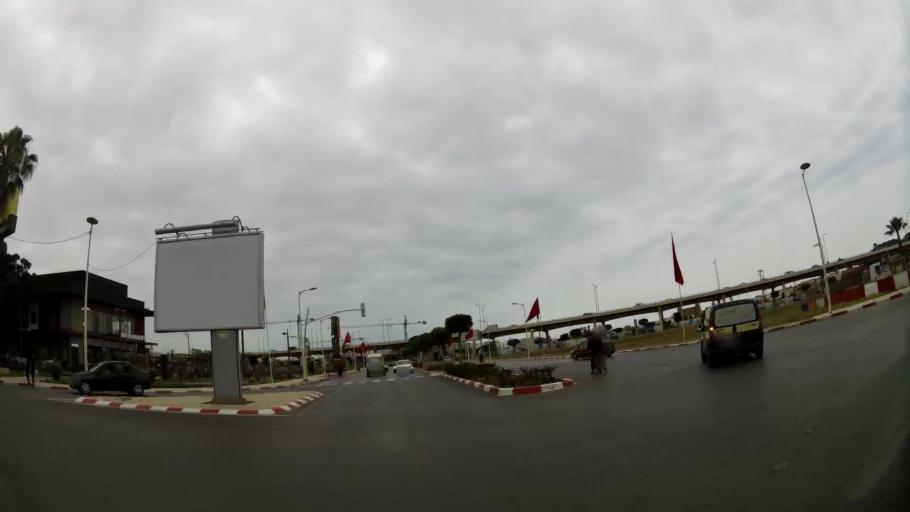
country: MA
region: Rabat-Sale-Zemmour-Zaer
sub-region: Rabat
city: Rabat
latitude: 34.0320
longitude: -6.8165
